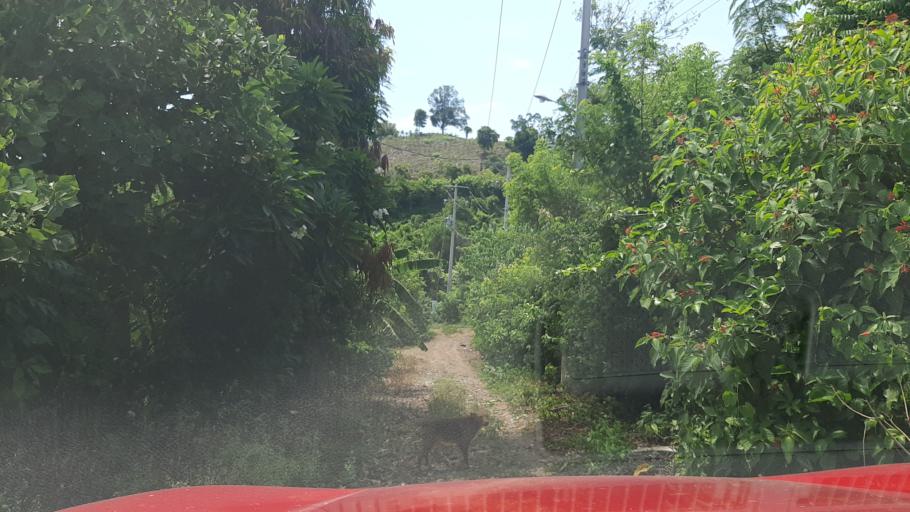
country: MX
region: Veracruz
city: Cazones de Herrera
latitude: 20.6768
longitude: -97.3231
